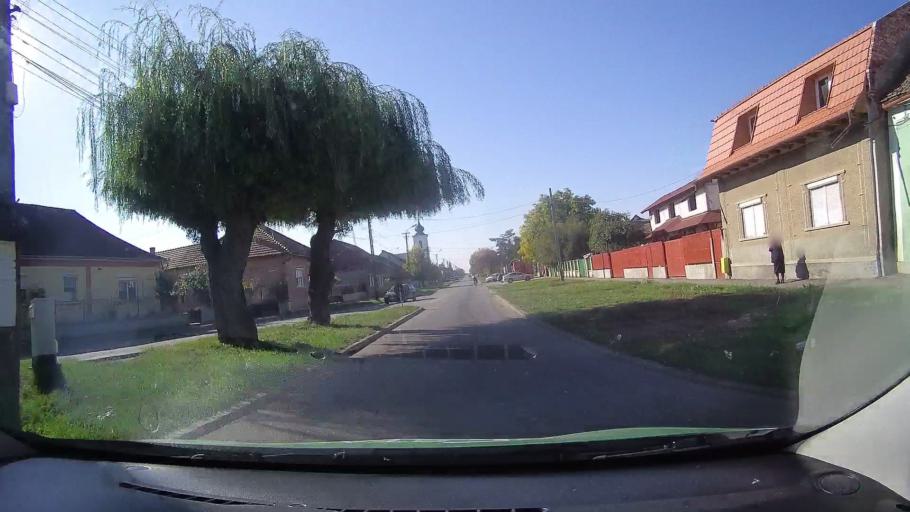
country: RO
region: Satu Mare
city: Carei
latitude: 47.6794
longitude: 22.4719
